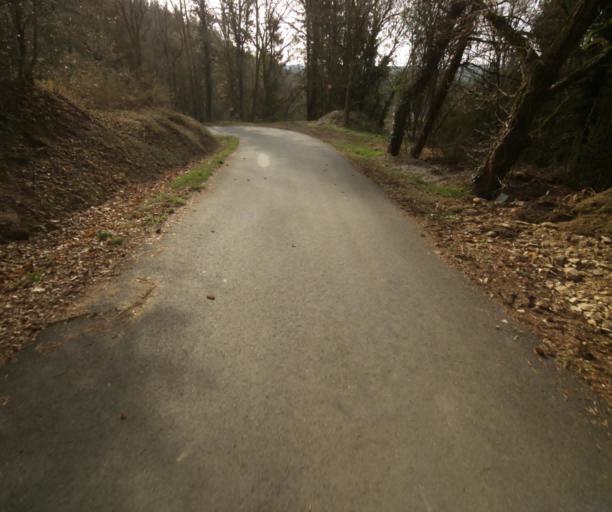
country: FR
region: Limousin
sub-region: Departement de la Correze
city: Chamboulive
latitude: 45.4350
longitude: 1.7866
